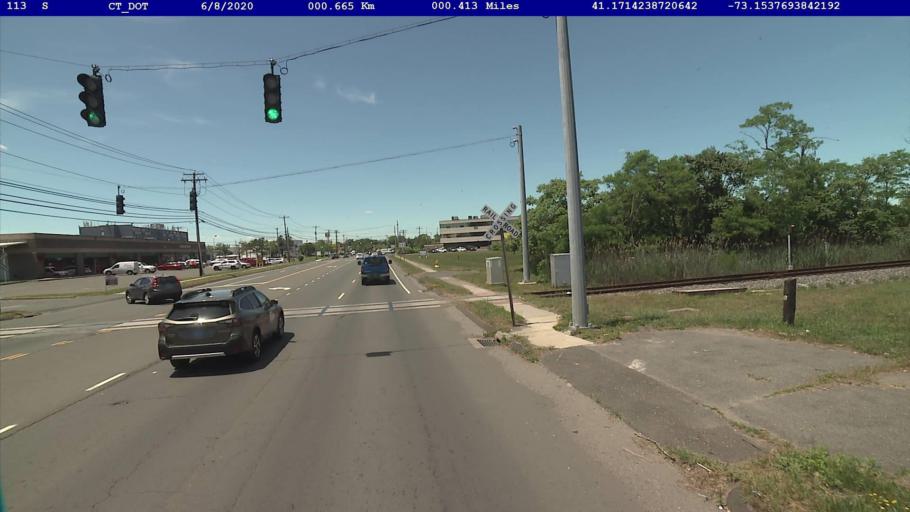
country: US
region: Connecticut
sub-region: Fairfield County
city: Stratford
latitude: 41.1714
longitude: -73.1538
